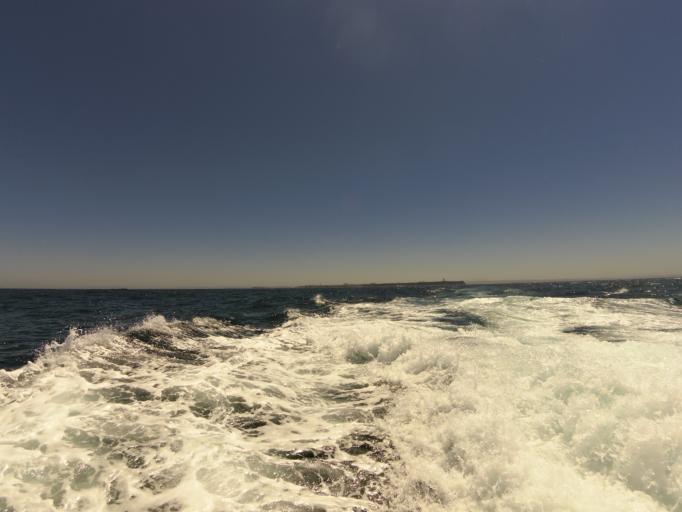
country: PT
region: Leiria
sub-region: Peniche
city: Peniche
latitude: 39.3734
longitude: -9.4382
